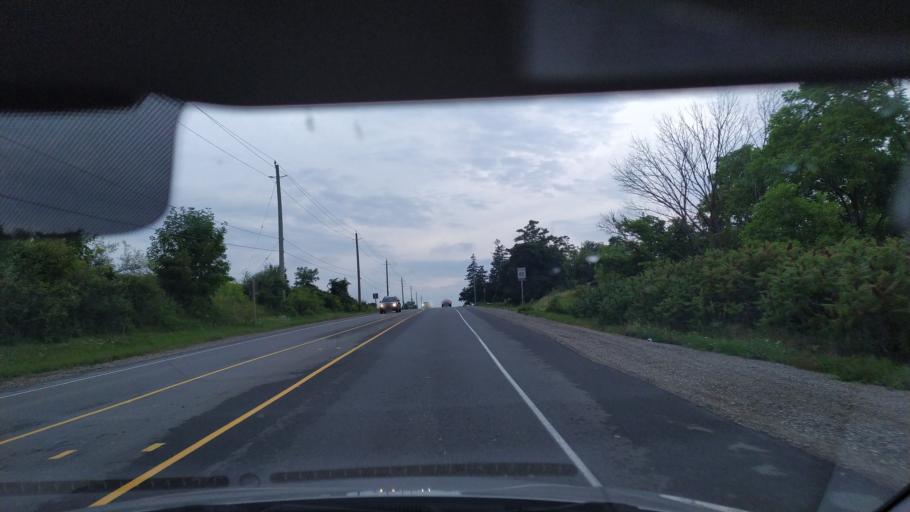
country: CA
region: Ontario
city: Cambridge
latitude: 43.3493
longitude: -80.3423
